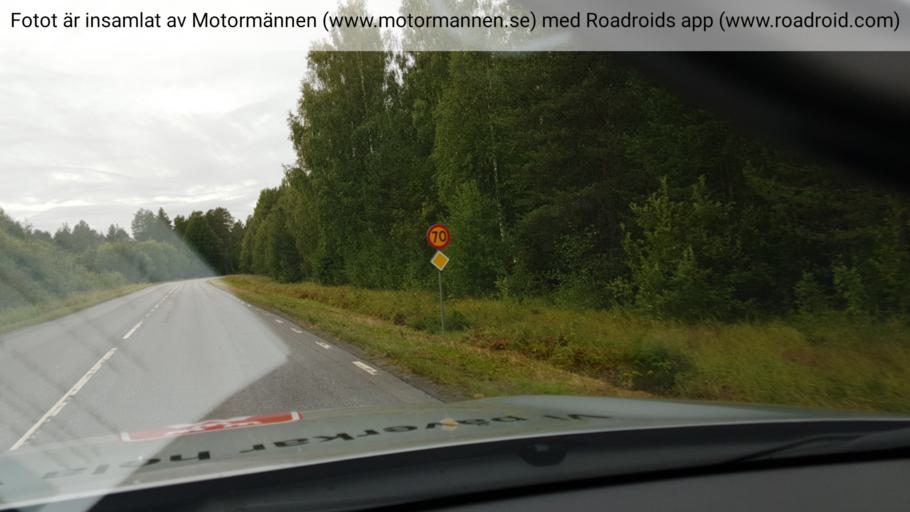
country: SE
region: Norrbotten
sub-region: Bodens Kommun
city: Boden
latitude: 65.8153
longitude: 21.6331
